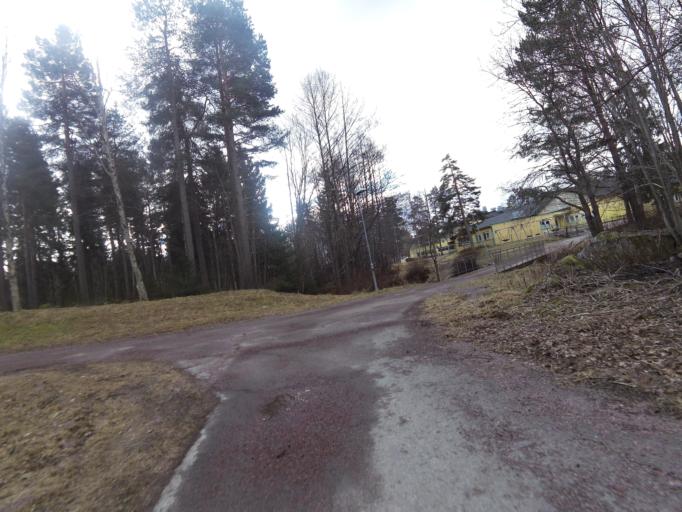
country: SE
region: Gaevleborg
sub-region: Gavle Kommun
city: Gavle
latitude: 60.6963
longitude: 17.1100
